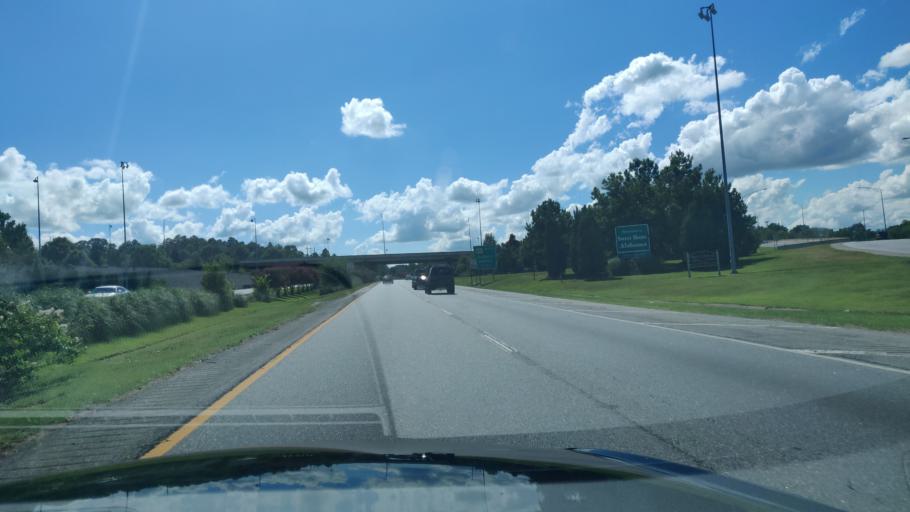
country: US
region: Georgia
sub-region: Muscogee County
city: Columbus
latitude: 32.4529
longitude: -84.9994
